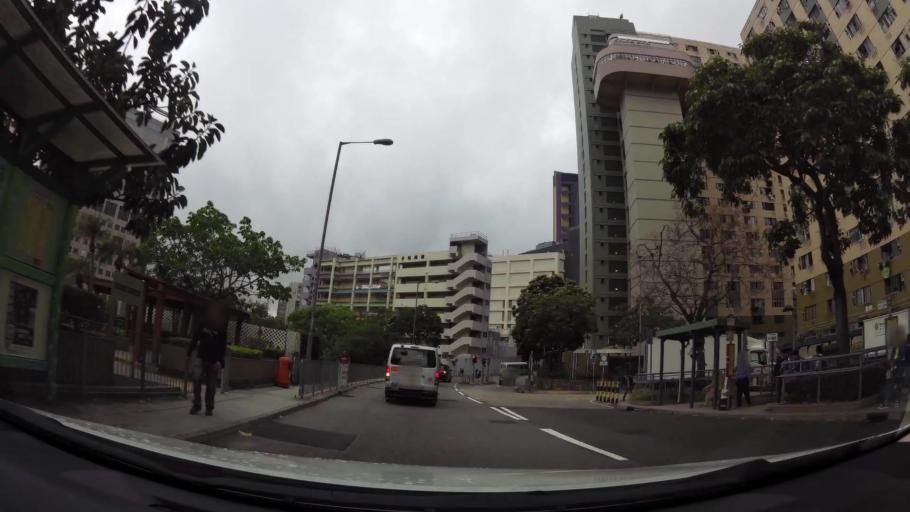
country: HK
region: Tsuen Wan
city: Tsuen Wan
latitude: 22.3596
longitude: 114.1225
